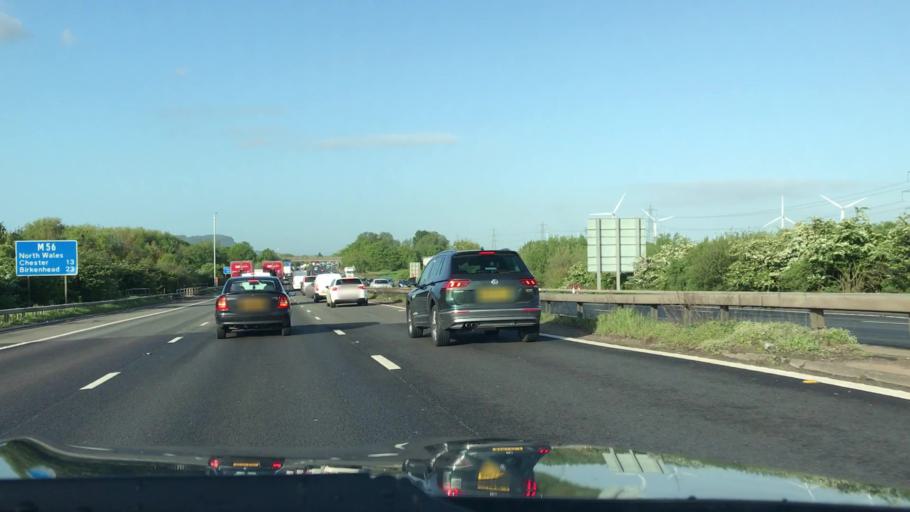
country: GB
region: England
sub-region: Cheshire West and Chester
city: Frodsham
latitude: 53.3054
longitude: -2.7161
